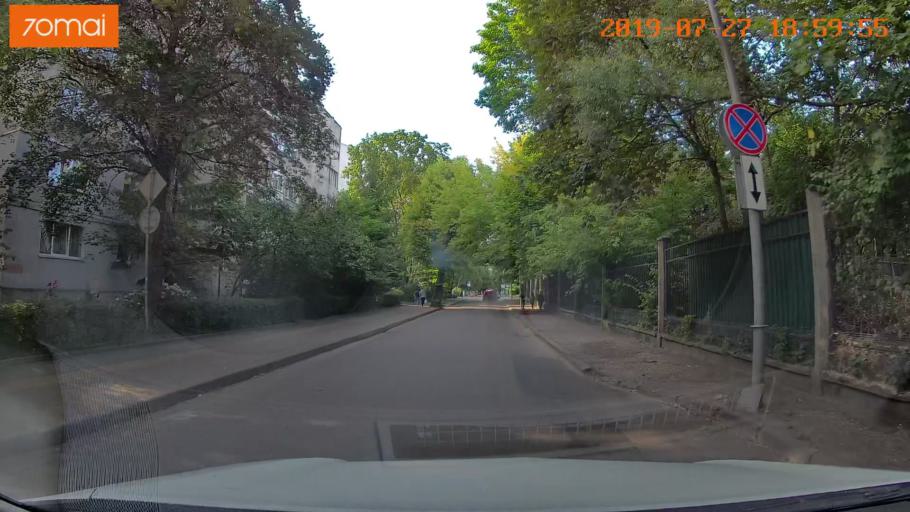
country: RU
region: Kaliningrad
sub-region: Gorod Kaliningrad
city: Kaliningrad
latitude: 54.7248
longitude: 20.4847
